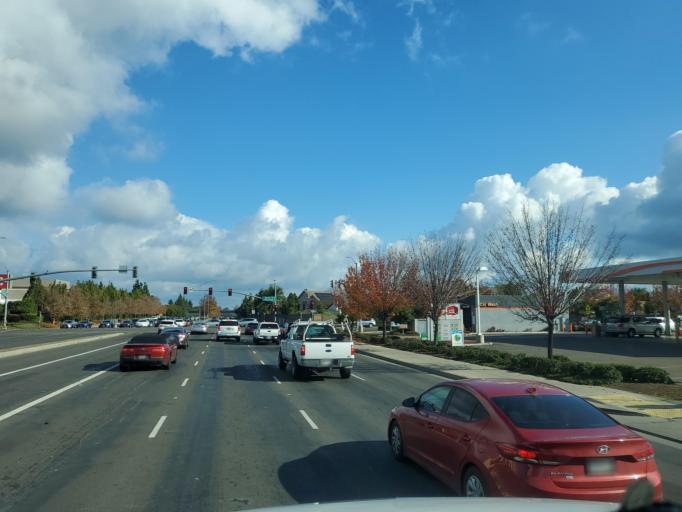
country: US
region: California
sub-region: San Joaquin County
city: August
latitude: 38.0033
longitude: -121.2856
